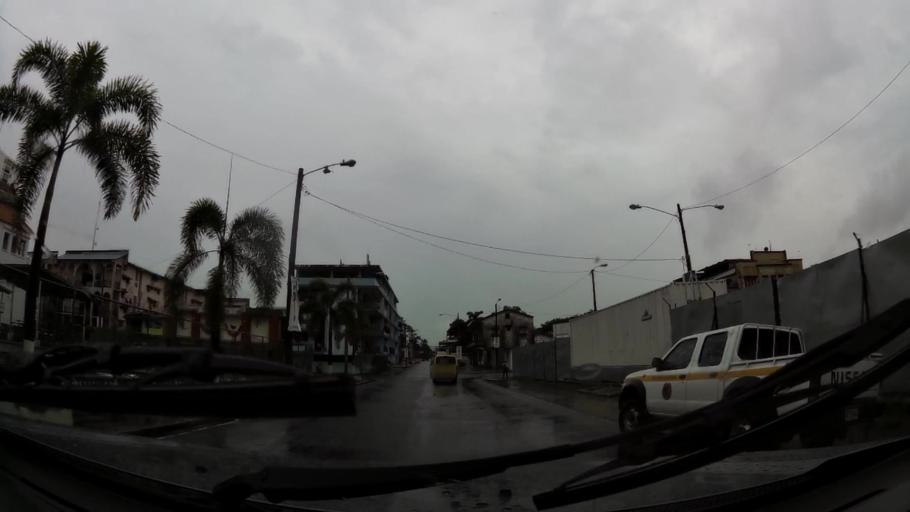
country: PA
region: Colon
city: Colon
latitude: 9.3602
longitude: -79.9040
